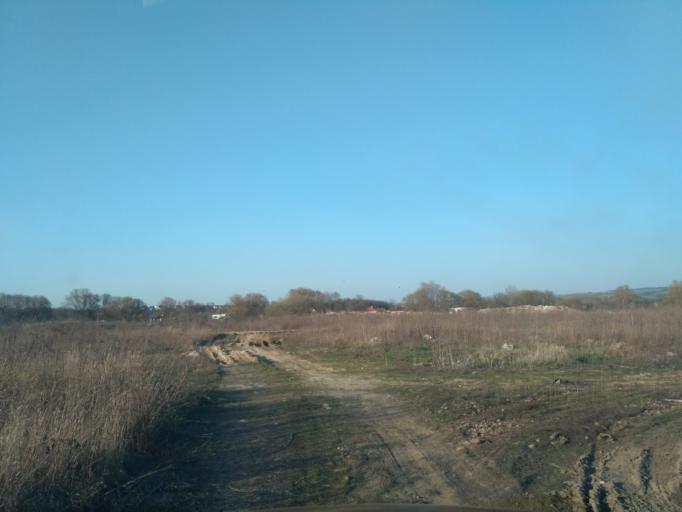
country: SK
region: Kosicky
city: Kosice
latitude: 48.6649
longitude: 21.3083
